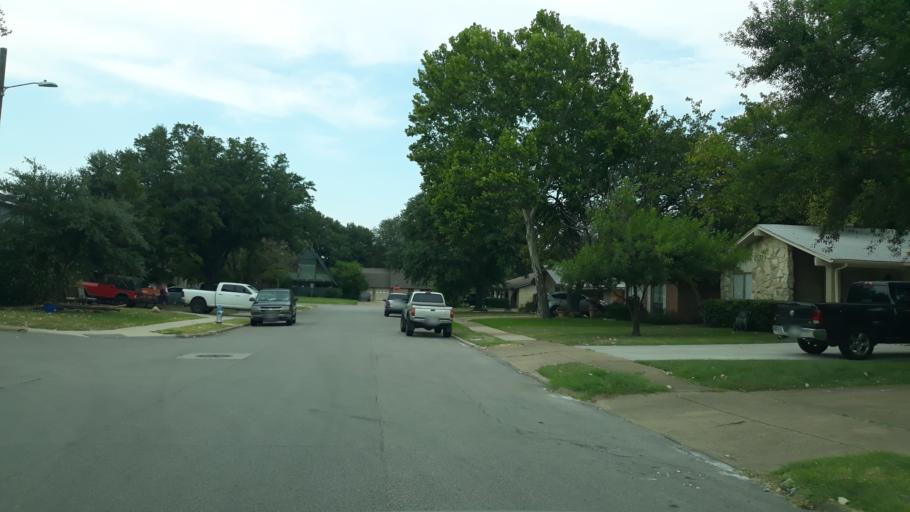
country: US
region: Texas
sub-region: Dallas County
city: Irving
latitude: 32.8428
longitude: -96.9869
